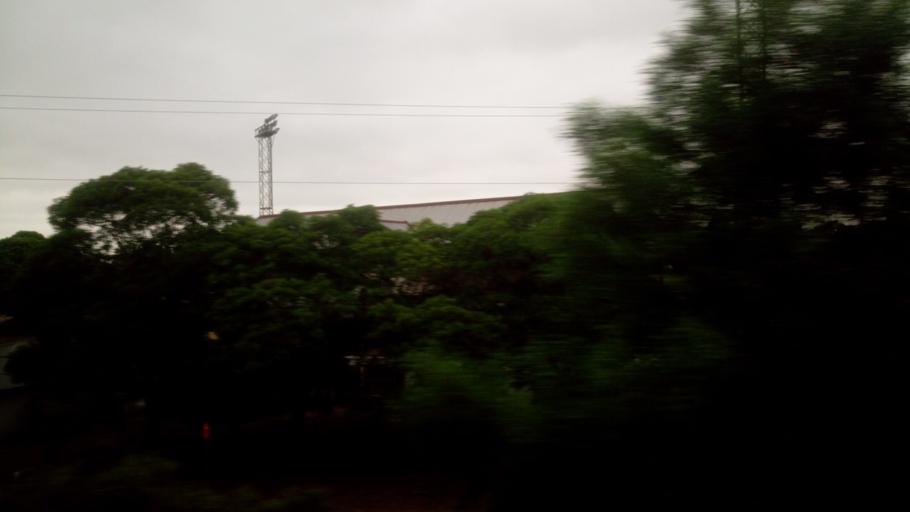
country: AU
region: New South Wales
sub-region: Auburn
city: Lidcombe
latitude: -33.8569
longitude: 151.0386
